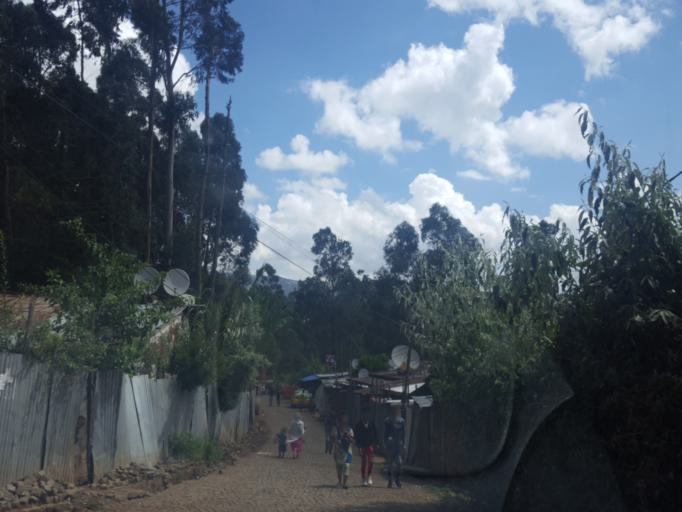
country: ET
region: Adis Abeba
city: Addis Ababa
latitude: 9.0615
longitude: 38.7640
